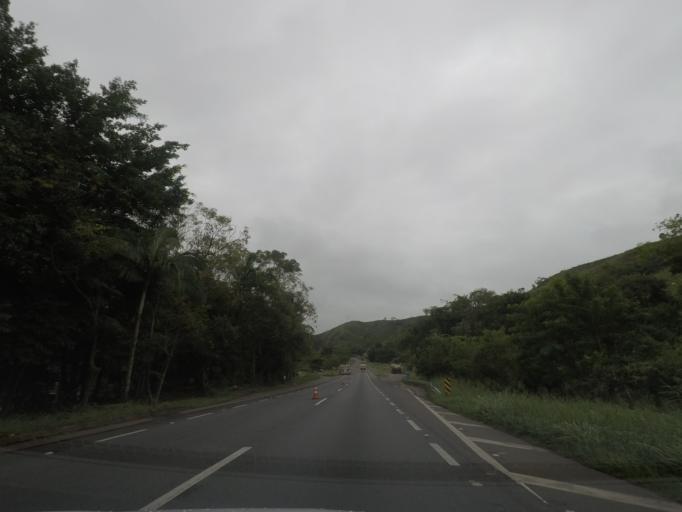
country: BR
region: Sao Paulo
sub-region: Cajati
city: Cajati
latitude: -24.8058
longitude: -48.2124
